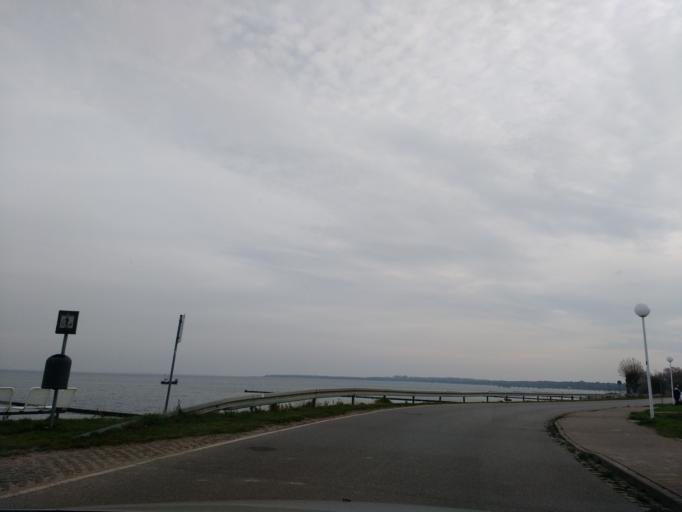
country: DE
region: Mecklenburg-Vorpommern
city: Ostseebad Boltenhagen
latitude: 53.9986
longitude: 11.1938
